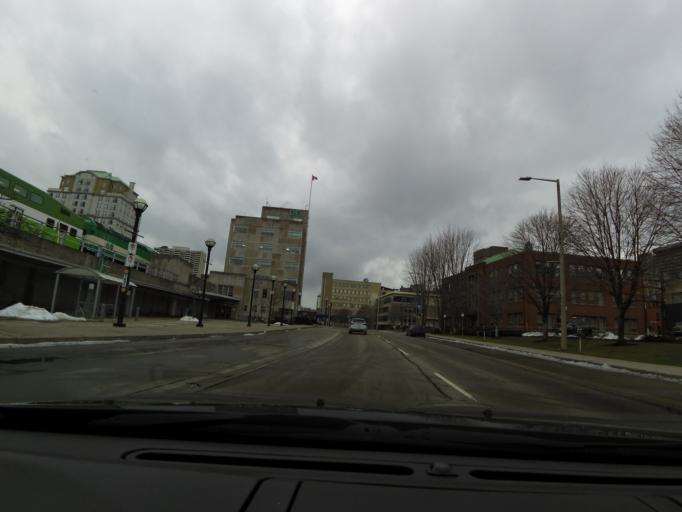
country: CA
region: Ontario
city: Hamilton
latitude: 43.2532
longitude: -79.8682
